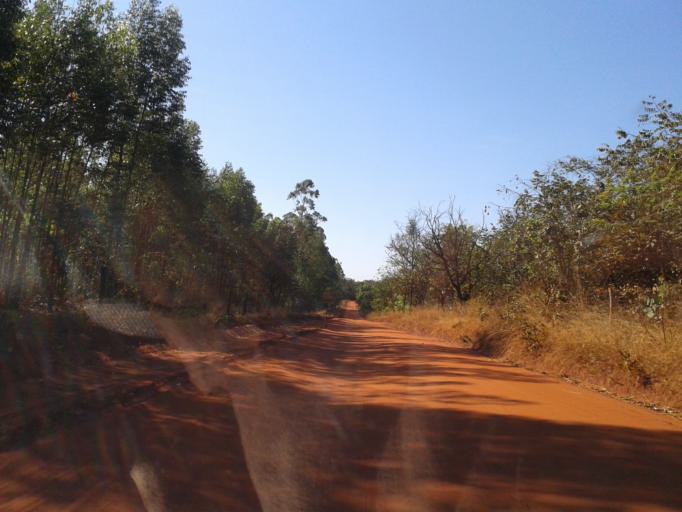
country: BR
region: Minas Gerais
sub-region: Ituiutaba
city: Ituiutaba
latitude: -19.0337
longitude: -49.3090
